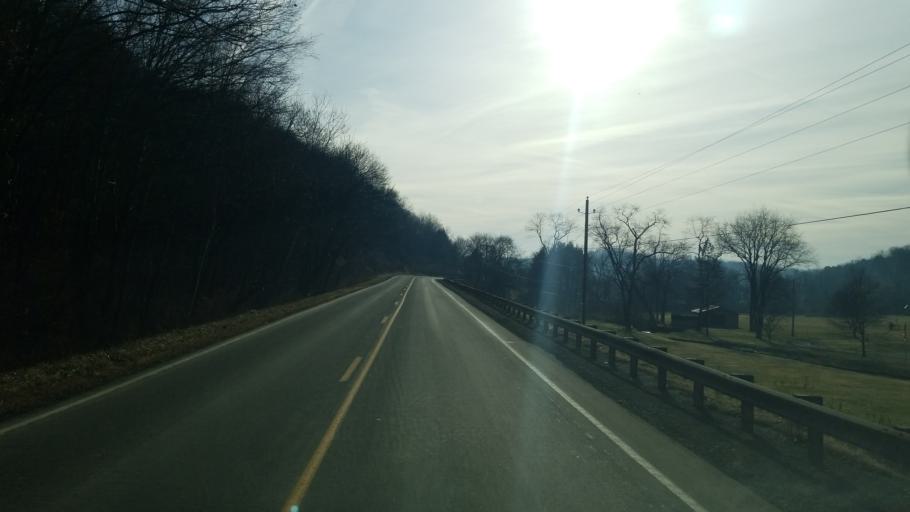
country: US
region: Pennsylvania
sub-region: Indiana County
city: Chevy Chase Heights
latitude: 40.7676
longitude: -79.1493
